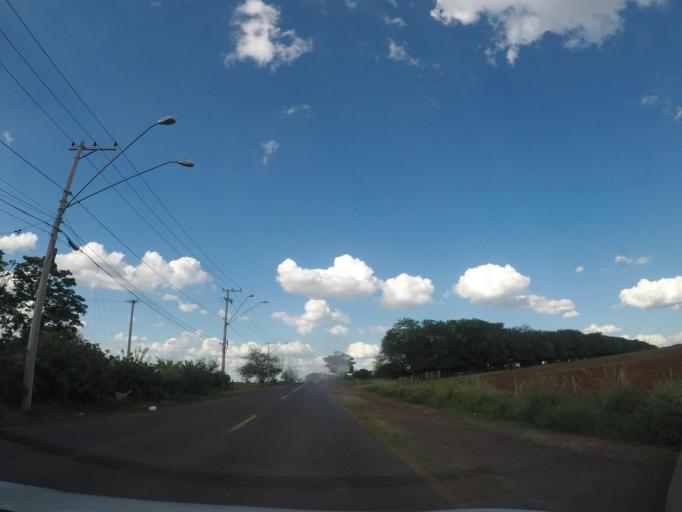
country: BR
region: Sao Paulo
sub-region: Sumare
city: Sumare
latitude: -22.8466
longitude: -47.2812
